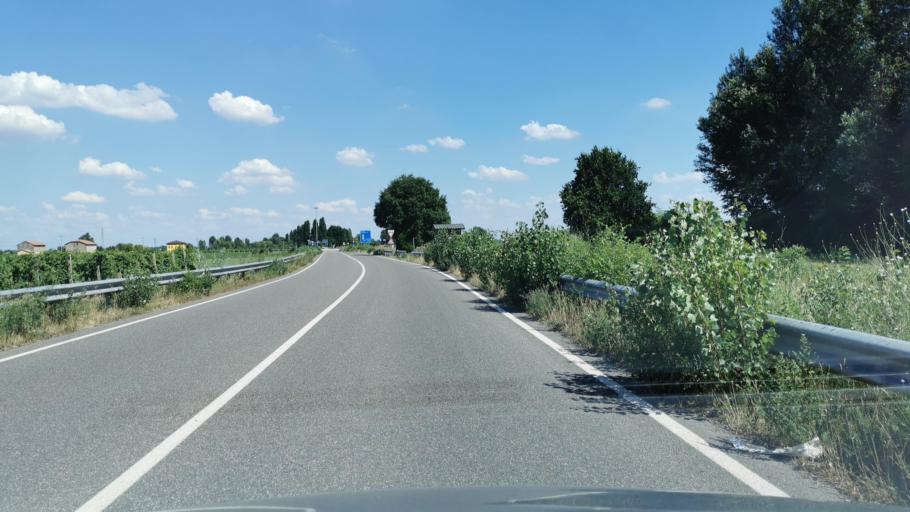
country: IT
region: Emilia-Romagna
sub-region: Provincia di Modena
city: Sam Marino
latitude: 44.7986
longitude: 10.9119
